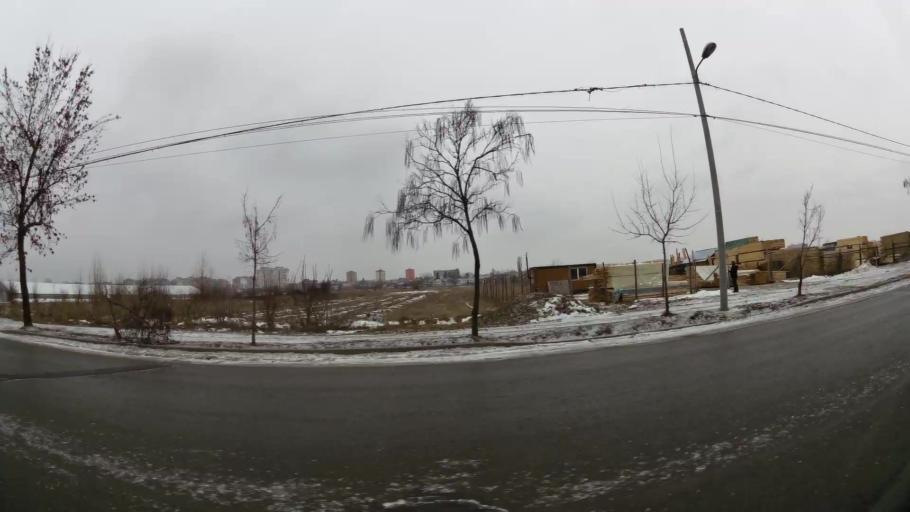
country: RO
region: Dambovita
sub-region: Municipiul Targoviste
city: Targoviste
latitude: 44.9274
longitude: 25.4818
